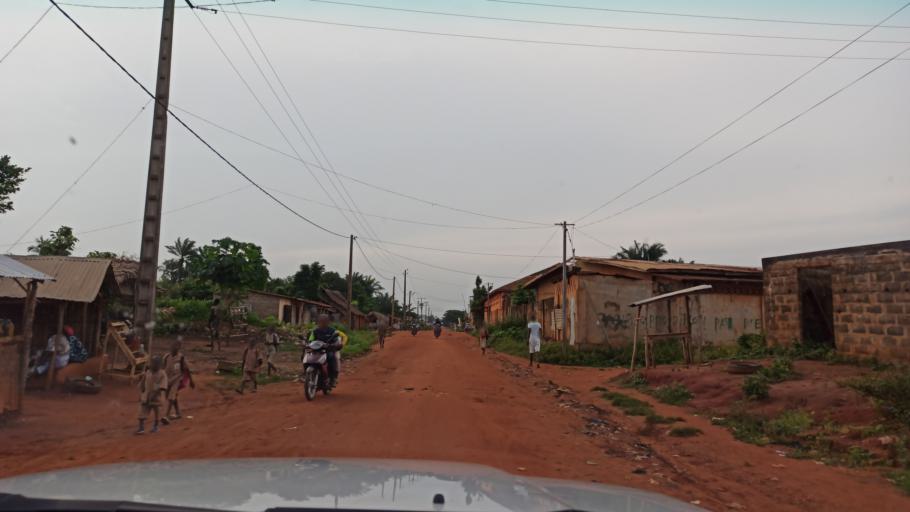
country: BJ
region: Queme
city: Porto-Novo
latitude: 6.5261
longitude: 2.6703
